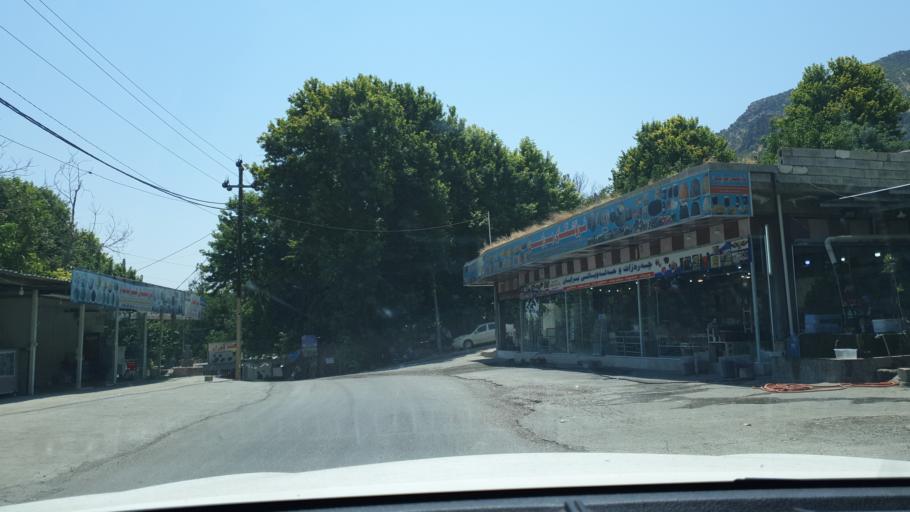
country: IQ
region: Arbil
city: Nahiyat Hiran
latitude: 36.2800
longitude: 44.4954
